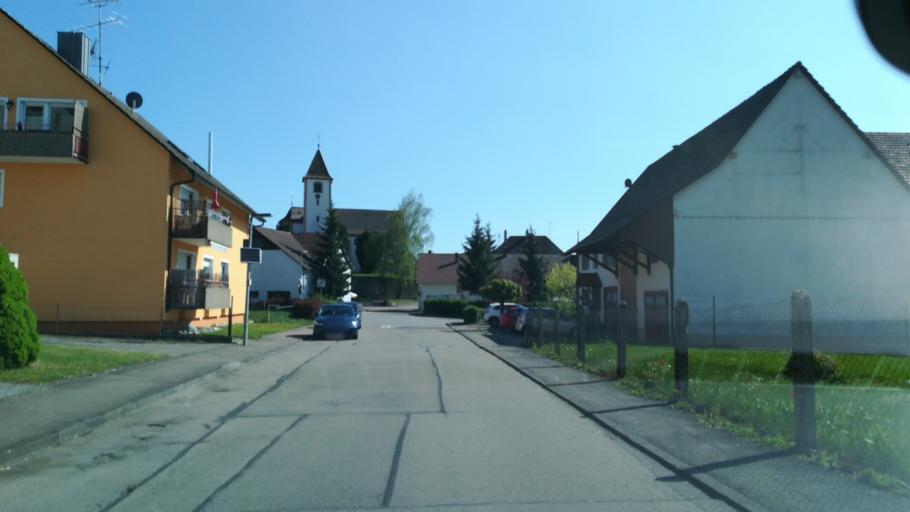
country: DE
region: Baden-Wuerttemberg
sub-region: Freiburg Region
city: Hilzingen
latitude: 47.7928
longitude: 8.7904
